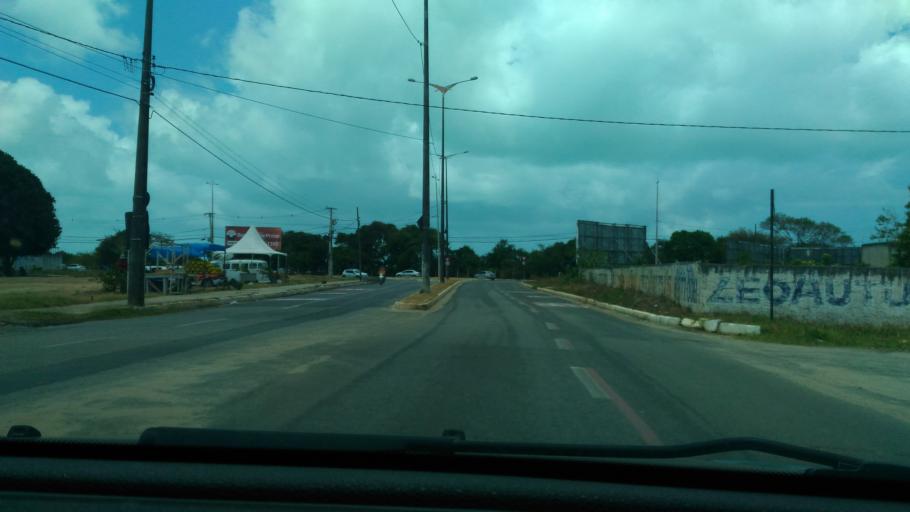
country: BR
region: Paraiba
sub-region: Joao Pessoa
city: Joao Pessoa
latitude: -7.1443
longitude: -34.8170
